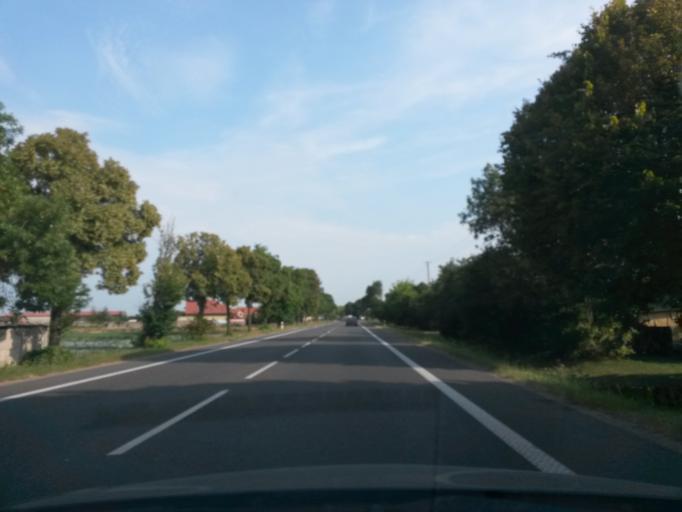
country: PL
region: Masovian Voivodeship
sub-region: Powiat sierpecki
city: Sierpc
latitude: 52.8570
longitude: 19.6825
